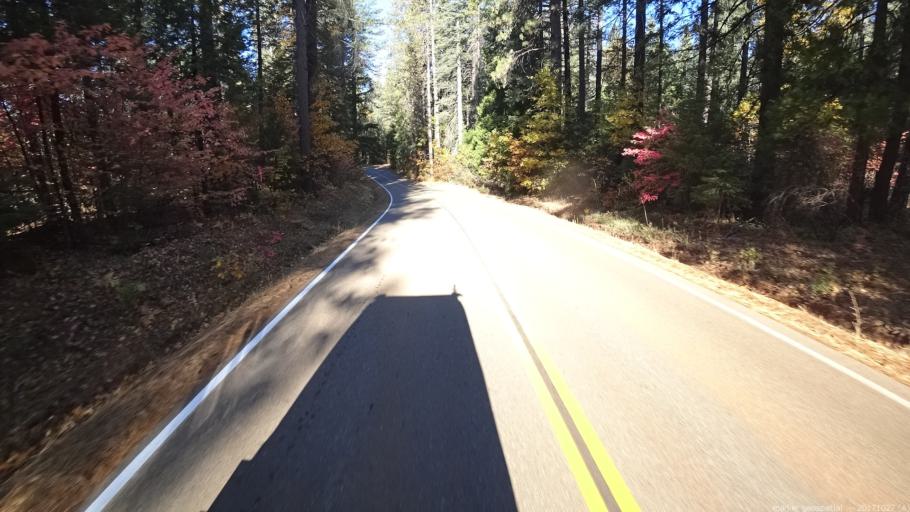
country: US
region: California
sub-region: Shasta County
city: Burney
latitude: 40.9280
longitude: -121.9350
